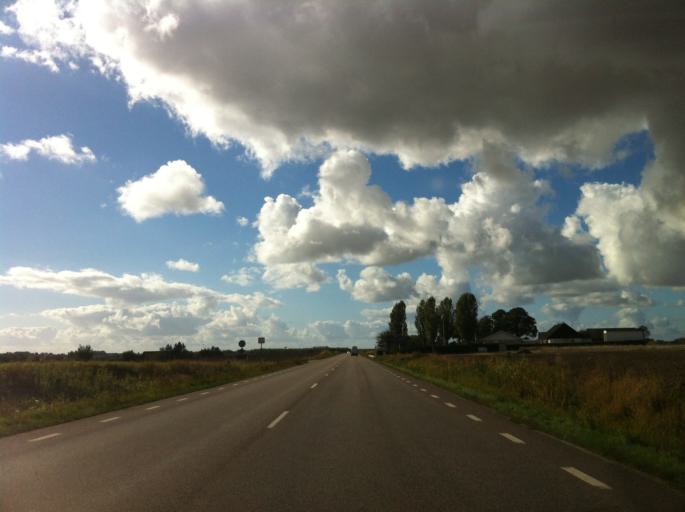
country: SE
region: Skane
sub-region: Kavlinge Kommun
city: Kaevlinge
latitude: 55.7958
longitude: 13.1985
